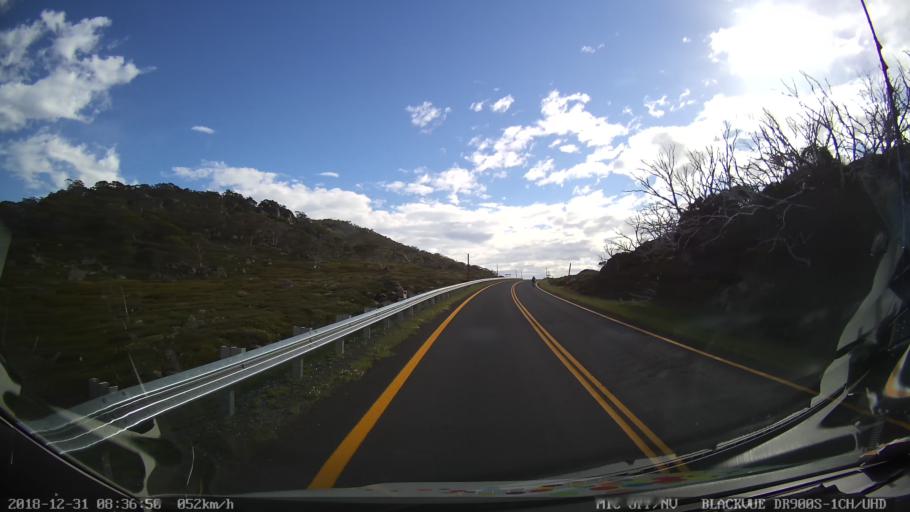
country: AU
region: New South Wales
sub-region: Snowy River
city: Jindabyne
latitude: -36.4221
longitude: 148.3796
